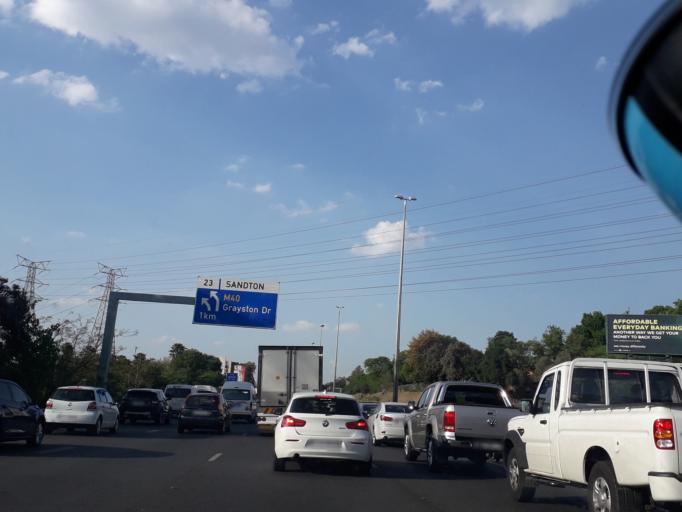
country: ZA
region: Gauteng
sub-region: City of Johannesburg Metropolitan Municipality
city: Johannesburg
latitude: -26.1207
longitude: 28.0728
